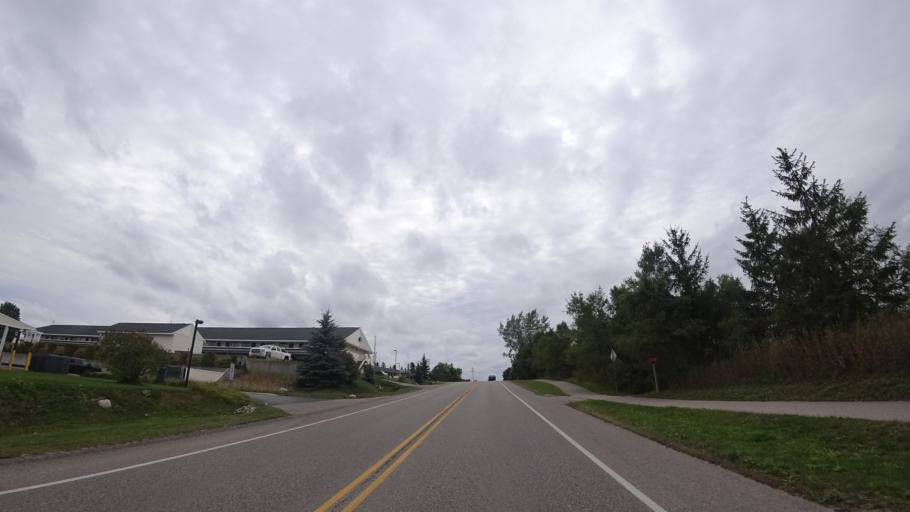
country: US
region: Michigan
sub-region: Emmet County
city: Petoskey
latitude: 45.3573
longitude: -84.9709
